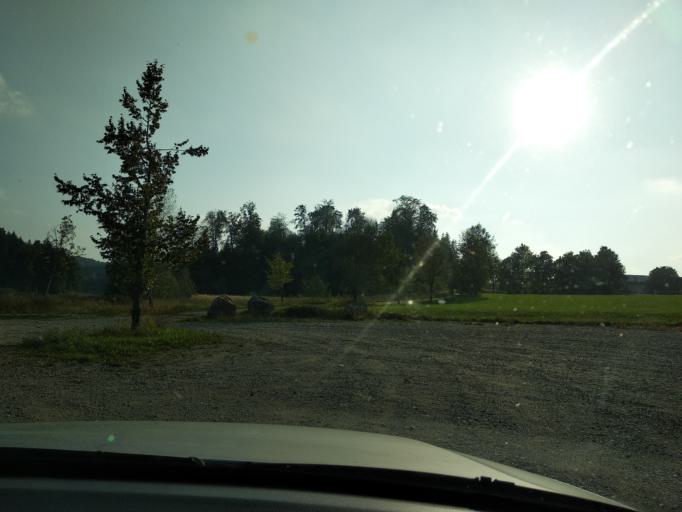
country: DE
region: Bavaria
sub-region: Upper Bavaria
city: Seeon-Seebruck
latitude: 47.9904
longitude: 12.4409
